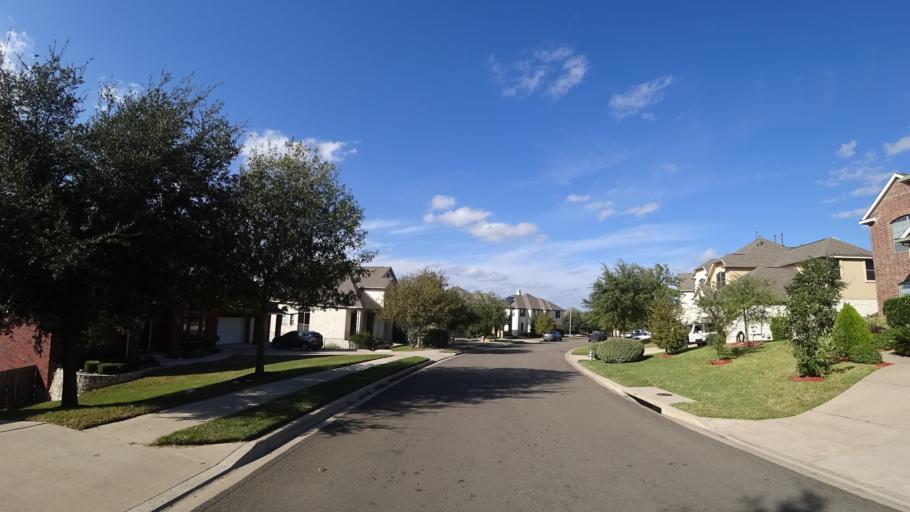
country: US
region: Texas
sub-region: Travis County
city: Barton Creek
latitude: 30.2481
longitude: -97.8779
